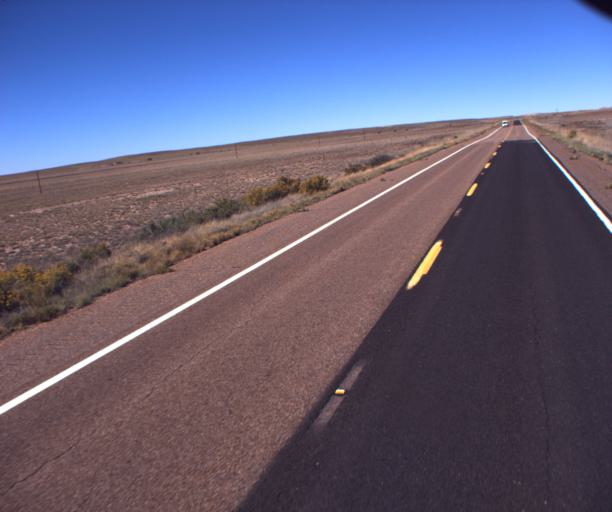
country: US
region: Arizona
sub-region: Navajo County
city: Snowflake
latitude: 34.7628
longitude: -109.8136
